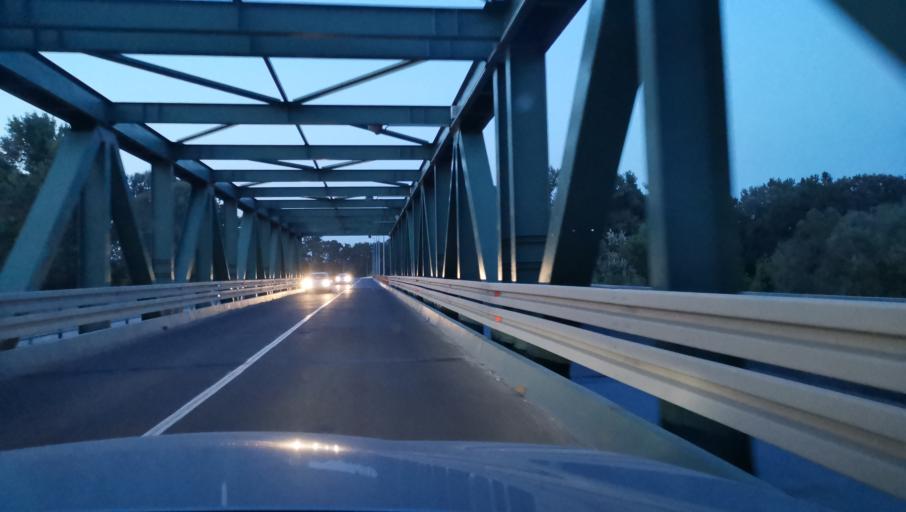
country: RS
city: Zvecka
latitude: 44.6744
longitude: 20.1674
